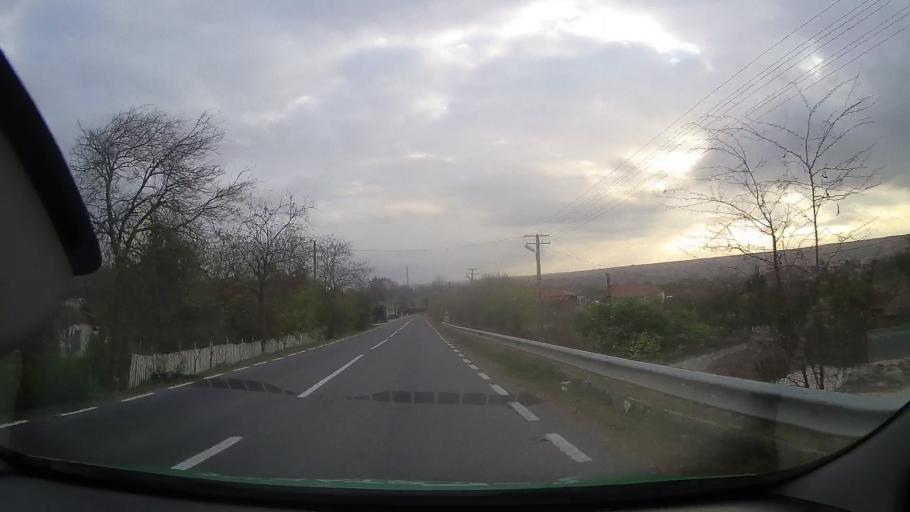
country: RO
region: Constanta
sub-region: Comuna Adamclisi
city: Adamclisi
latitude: 44.0874
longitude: 27.9610
